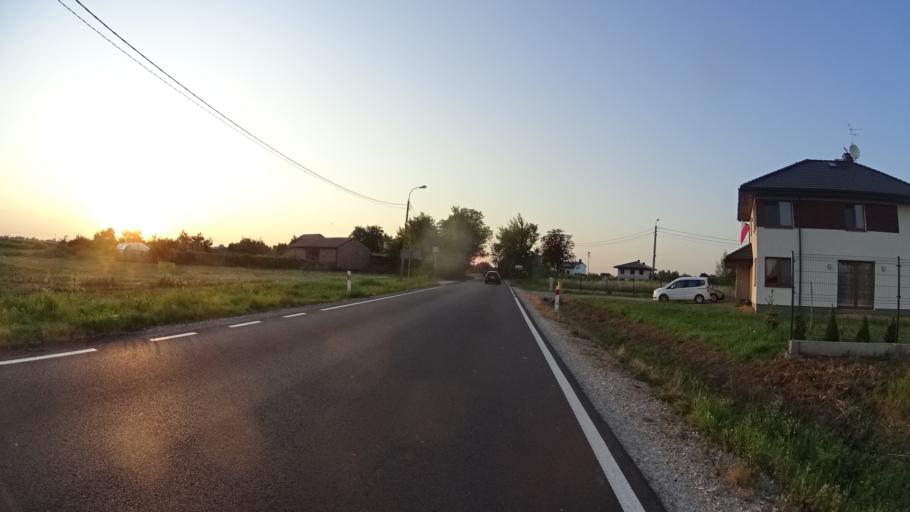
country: PL
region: Masovian Voivodeship
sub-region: Powiat warszawski zachodni
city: Ozarow Mazowiecki
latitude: 52.2458
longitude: 20.7462
